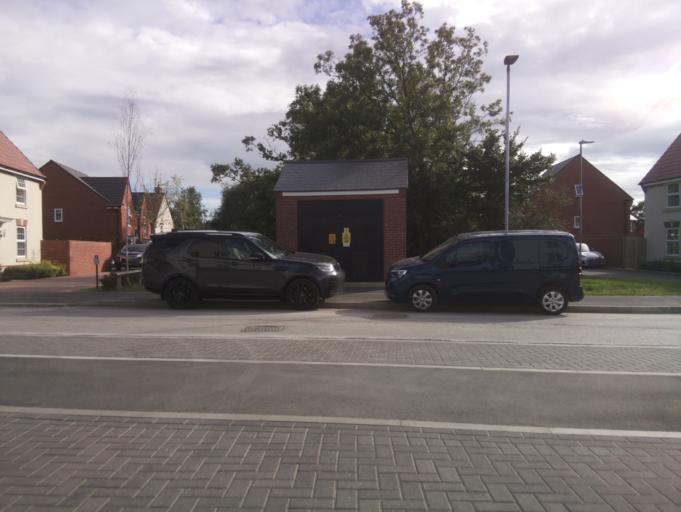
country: GB
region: England
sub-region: Gloucestershire
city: Stonehouse
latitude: 51.8058
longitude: -2.2694
